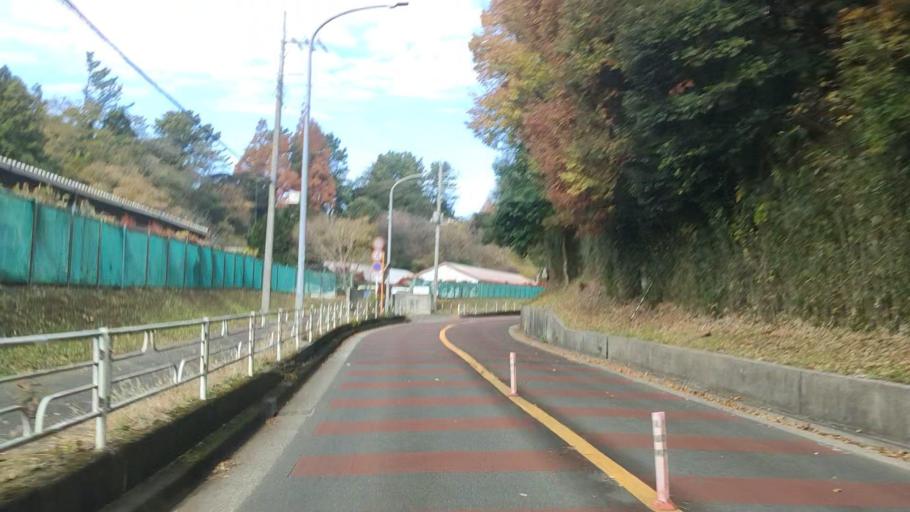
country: JP
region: Kanagawa
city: Yokohama
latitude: 35.4404
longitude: 139.5446
